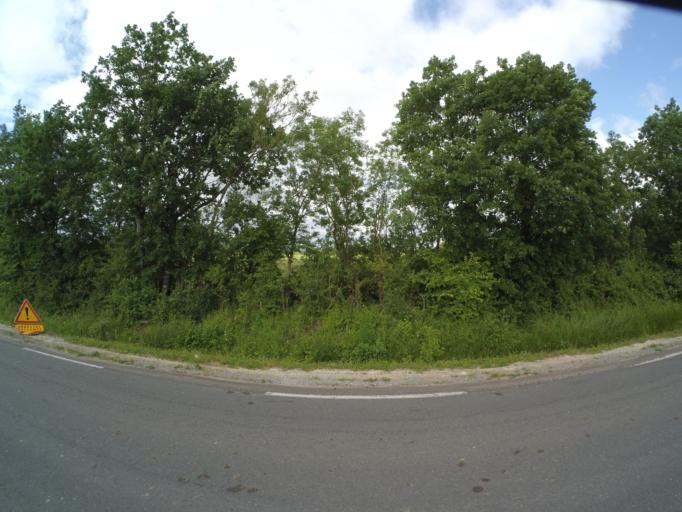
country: FR
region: Aquitaine
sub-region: Departement de la Gironde
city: Saint-Louis-de-Montferrand
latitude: 44.9728
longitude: -0.5569
